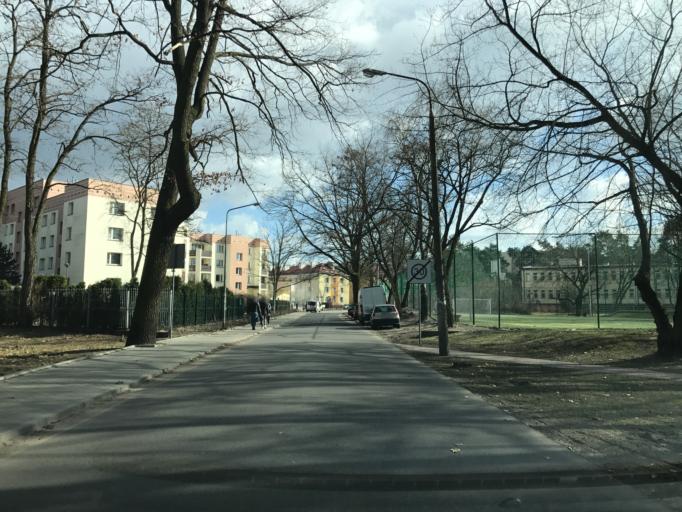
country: PL
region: Masovian Voivodeship
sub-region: Warszawa
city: Rembertow
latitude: 52.2631
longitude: 21.1767
